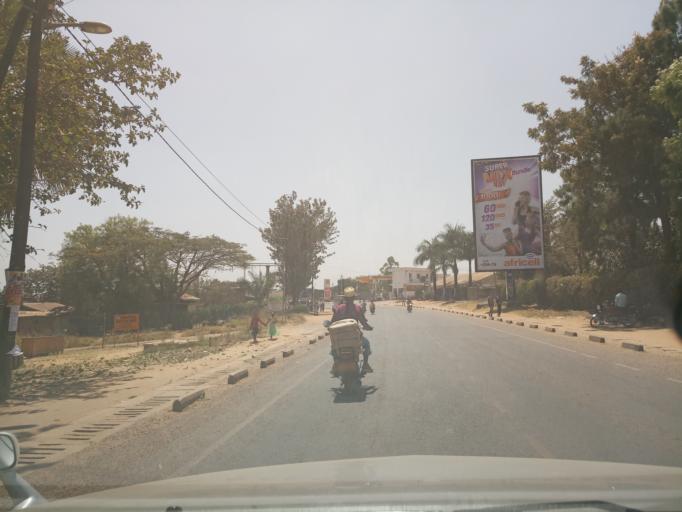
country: UG
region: Northern Region
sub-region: Arua District
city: Arua
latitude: 3.0096
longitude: 30.9118
